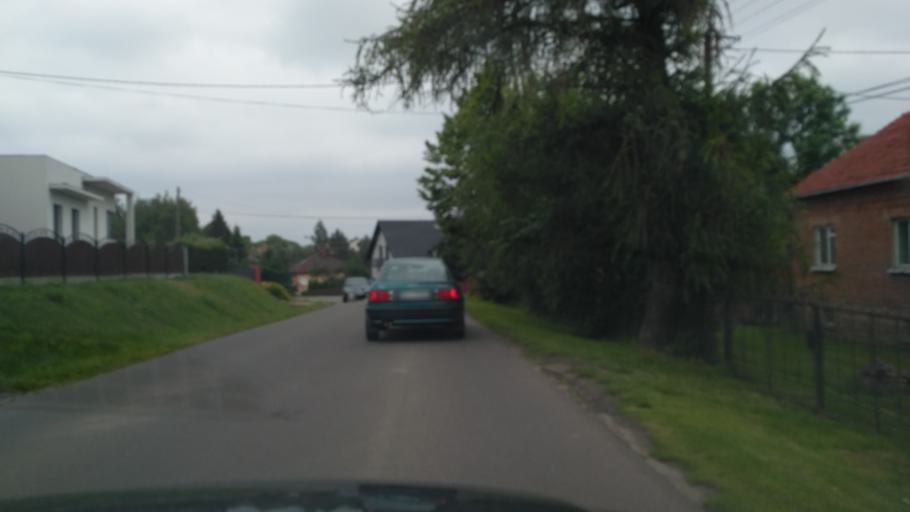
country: PL
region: Subcarpathian Voivodeship
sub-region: Powiat ropczycko-sedziszowski
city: Zagorzyce
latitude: 50.0354
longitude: 21.6922
